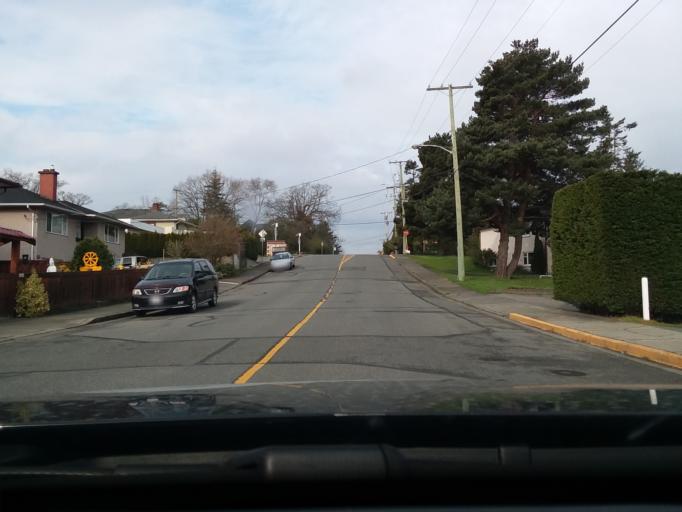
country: CA
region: British Columbia
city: Victoria
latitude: 48.4388
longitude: -123.4008
